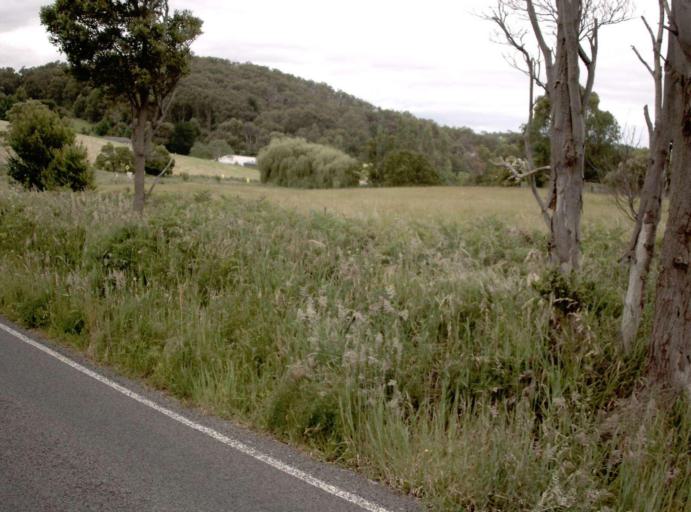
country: AU
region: Victoria
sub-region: Bass Coast
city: North Wonthaggi
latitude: -38.5138
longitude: 145.7169
